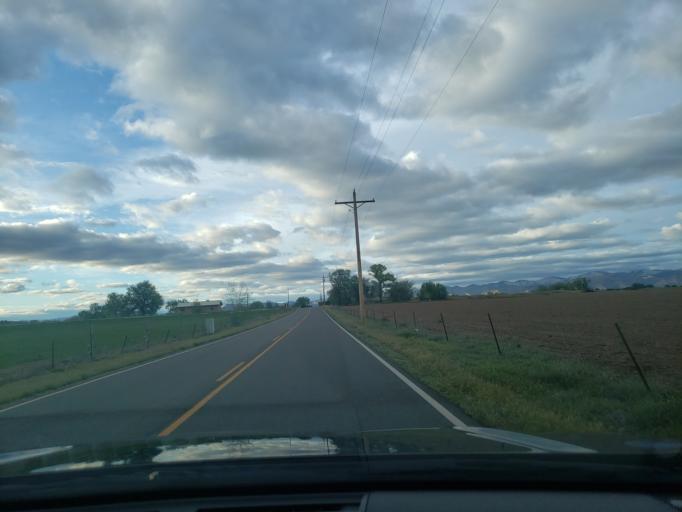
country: US
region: Colorado
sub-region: Mesa County
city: Fruita
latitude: 39.1988
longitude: -108.7291
